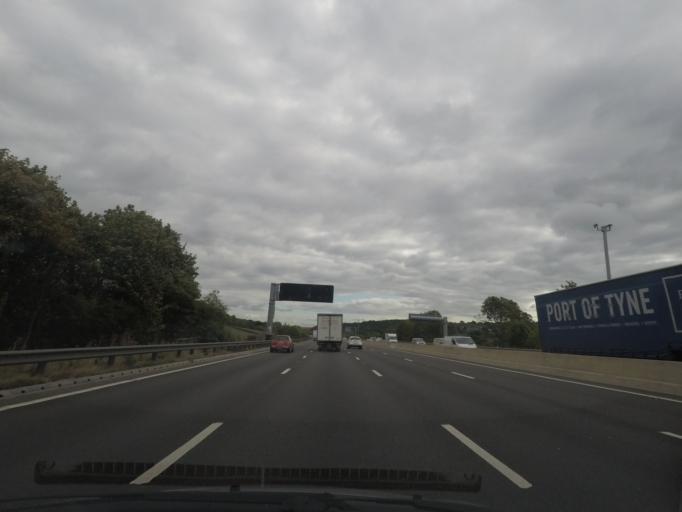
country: GB
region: England
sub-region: Rotherham
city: Wentworth
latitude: 53.4429
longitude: -1.4394
